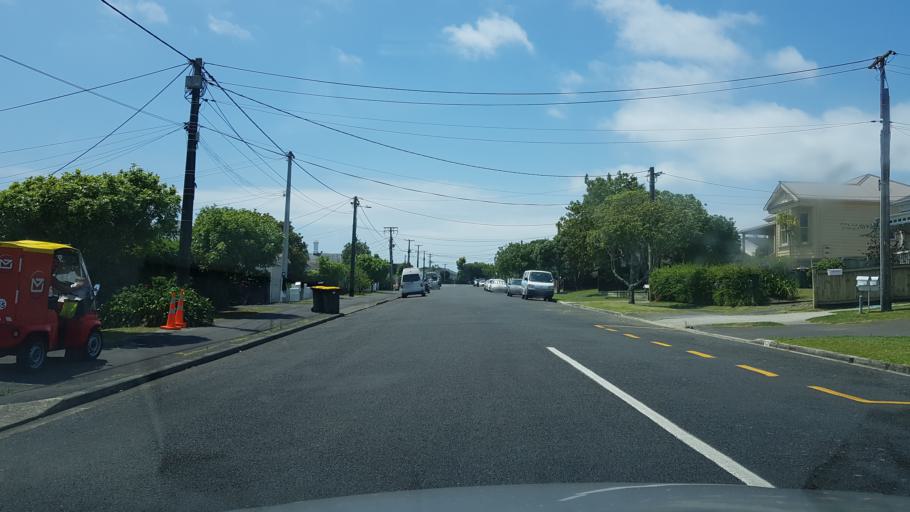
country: NZ
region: Auckland
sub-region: Auckland
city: North Shore
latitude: -36.8143
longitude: 174.7902
